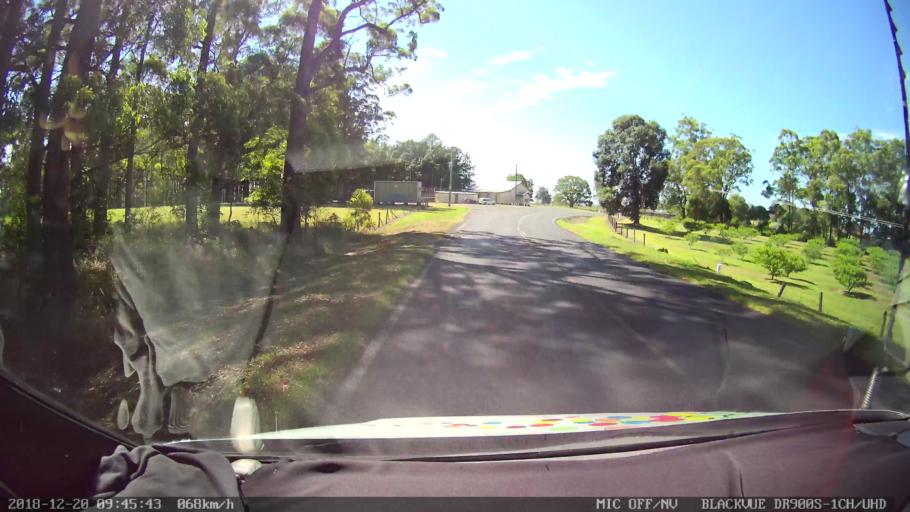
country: AU
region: New South Wales
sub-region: Lismore Municipality
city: Lismore
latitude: -28.7461
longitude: 153.3023
